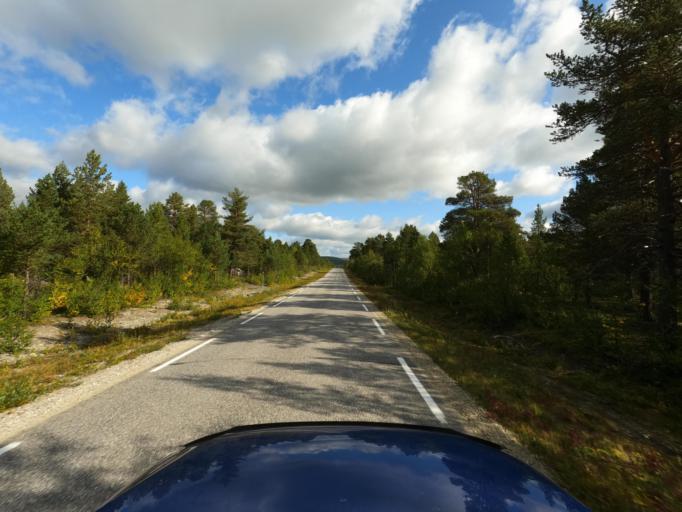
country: NO
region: Finnmark Fylke
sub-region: Karasjok
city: Karasjohka
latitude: 69.4324
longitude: 24.9717
